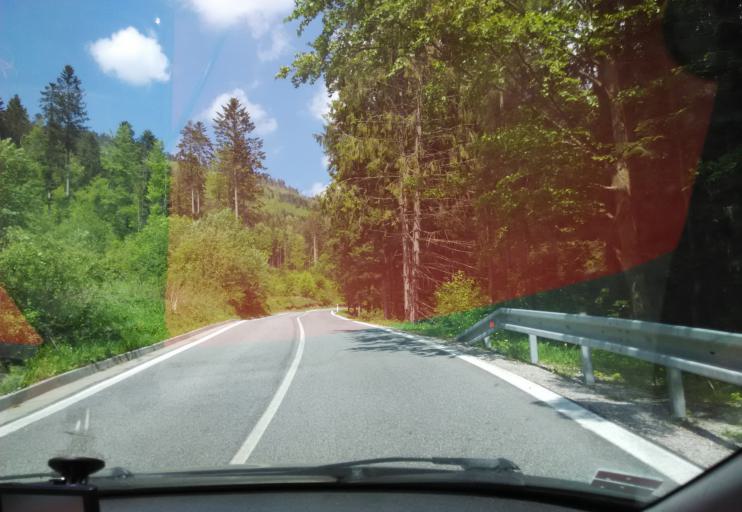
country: SK
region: Kosicky
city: Dobsina
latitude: 48.8514
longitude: 20.4543
